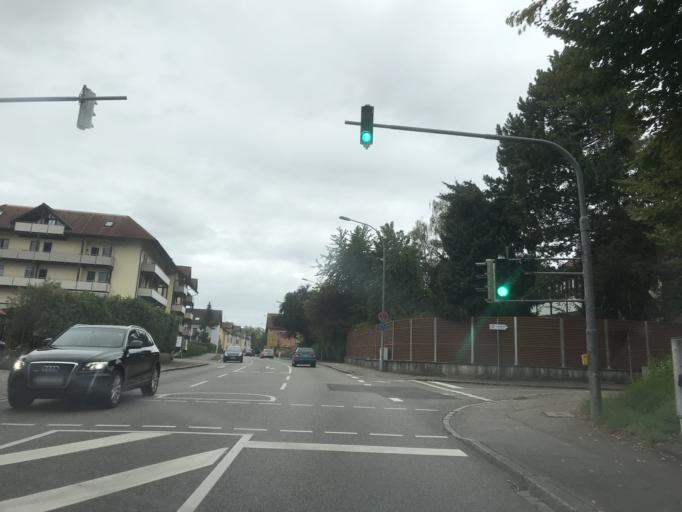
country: DE
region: Baden-Wuerttemberg
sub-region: Freiburg Region
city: Bad Sackingen
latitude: 47.5582
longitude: 7.9514
